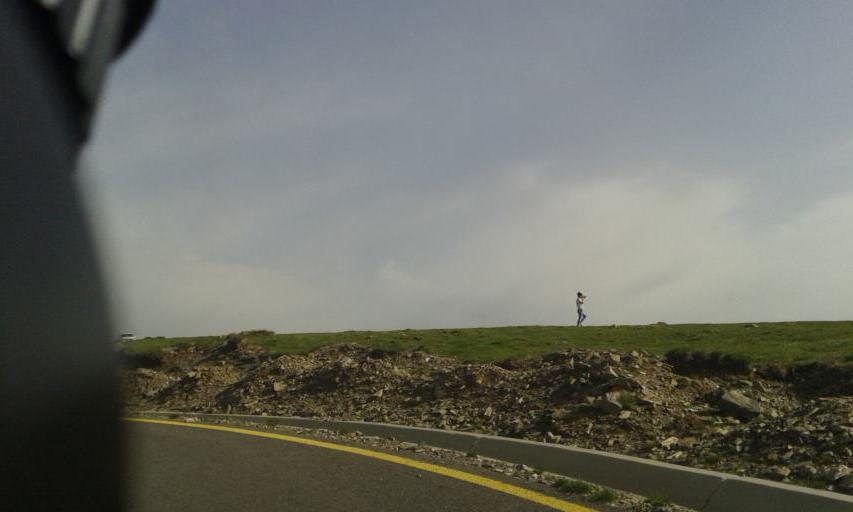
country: RO
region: Gorj
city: Novaci-Straini
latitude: 45.3662
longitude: 23.6496
